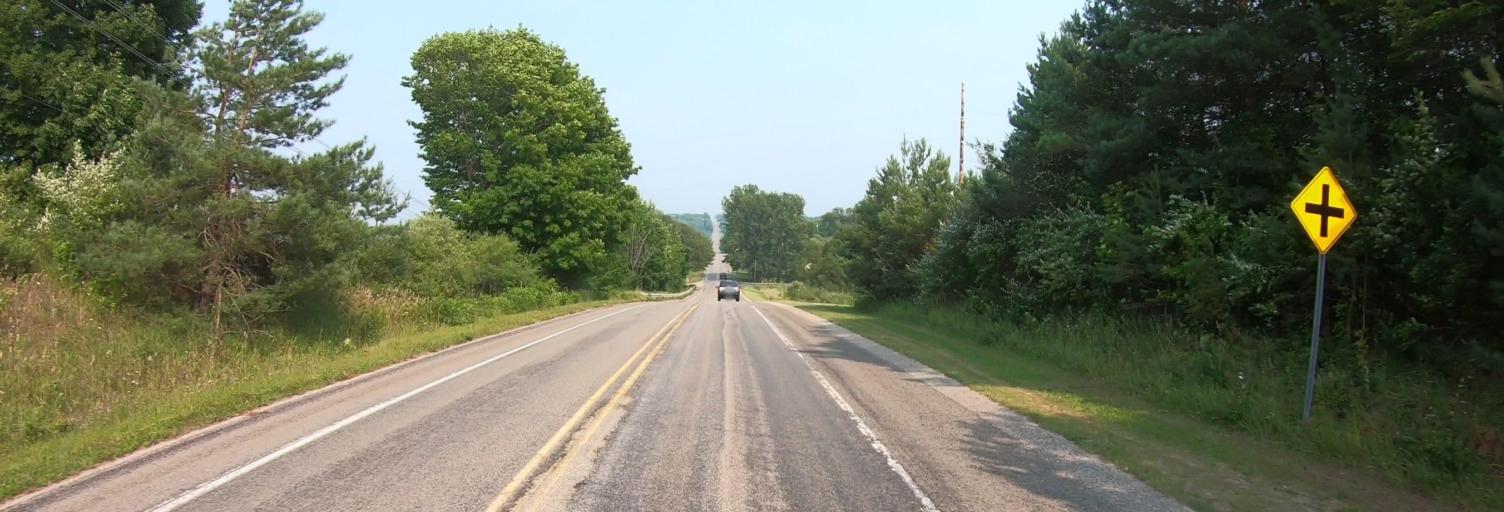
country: US
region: Michigan
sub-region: Charlevoix County
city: Charlevoix
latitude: 45.1857
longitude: -85.3270
